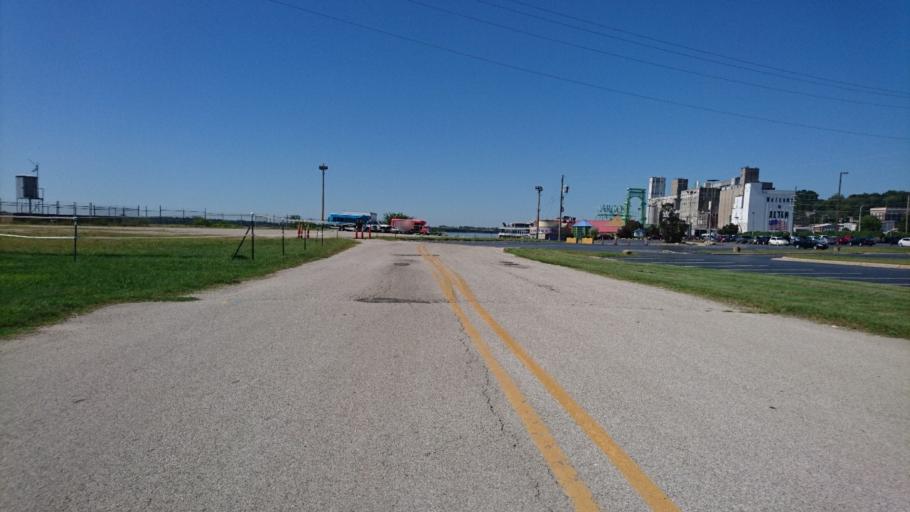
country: US
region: Illinois
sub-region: Madison County
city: Alton
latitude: 38.8876
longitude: -90.1833
